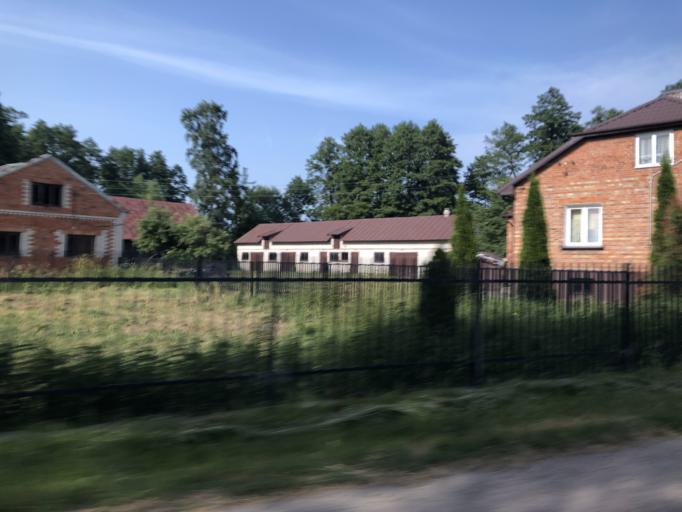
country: PL
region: Podlasie
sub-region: Lomza
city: Lomza
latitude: 53.1446
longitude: 22.0102
